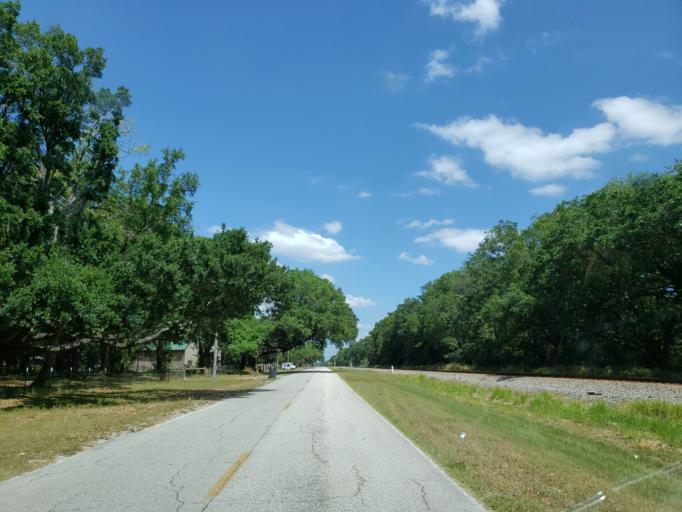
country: US
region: Florida
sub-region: Hillsborough County
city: Dover
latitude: 27.9627
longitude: -82.2103
